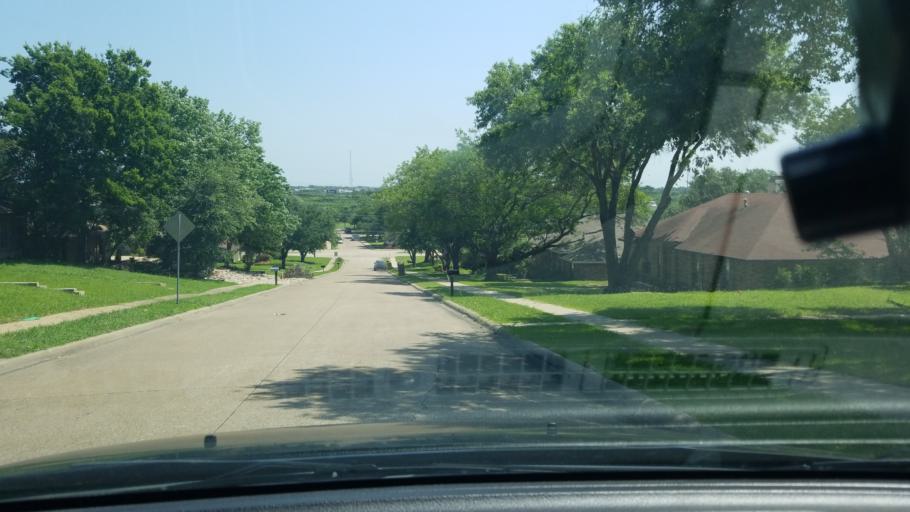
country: US
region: Texas
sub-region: Dallas County
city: Sunnyvale
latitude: 32.8306
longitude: -96.6036
